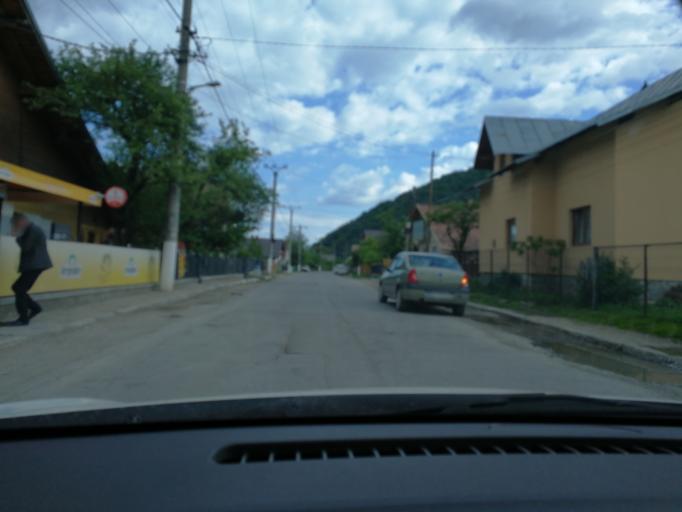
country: RO
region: Prahova
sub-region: Comuna Valea Doftanei
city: Tesila
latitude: 45.2895
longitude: 25.7229
